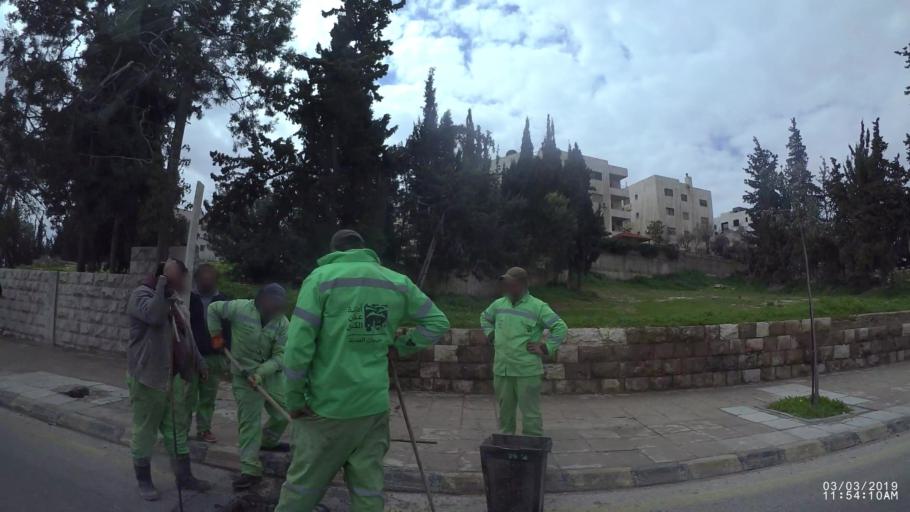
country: JO
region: Amman
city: Amman
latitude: 31.9833
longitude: 35.9006
